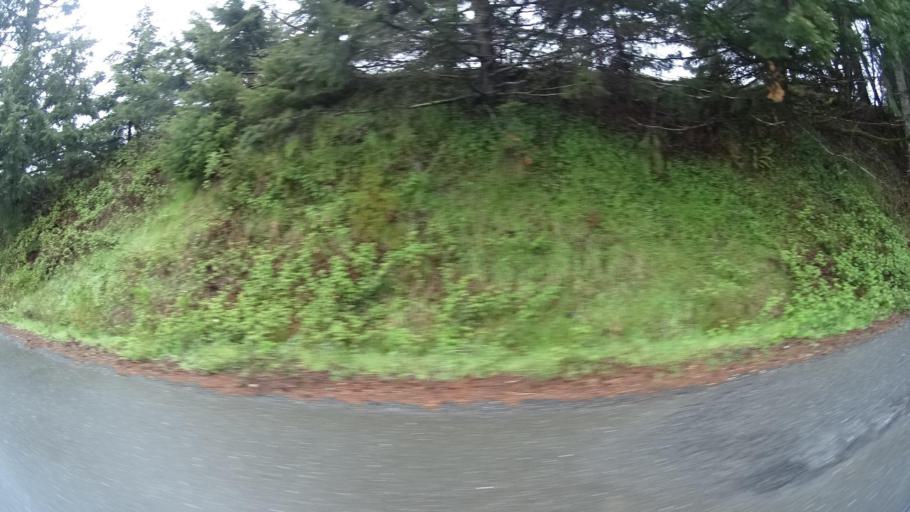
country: US
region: California
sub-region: Humboldt County
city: Westhaven-Moonstone
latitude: 41.1841
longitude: -123.9256
